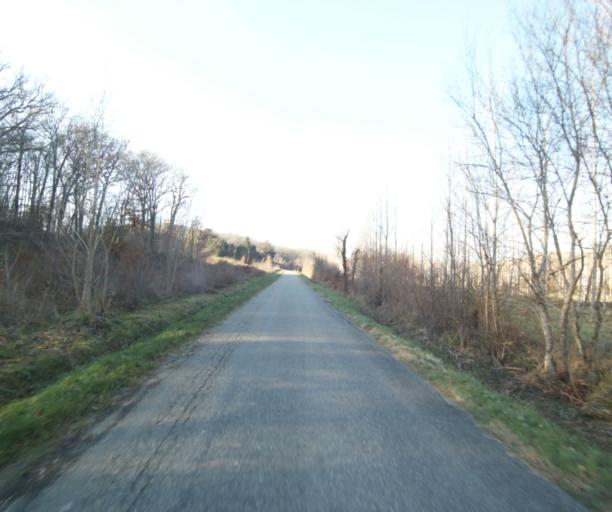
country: FR
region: Midi-Pyrenees
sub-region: Departement du Tarn-et-Garonne
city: Moissac
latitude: 44.1261
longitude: 1.0950
